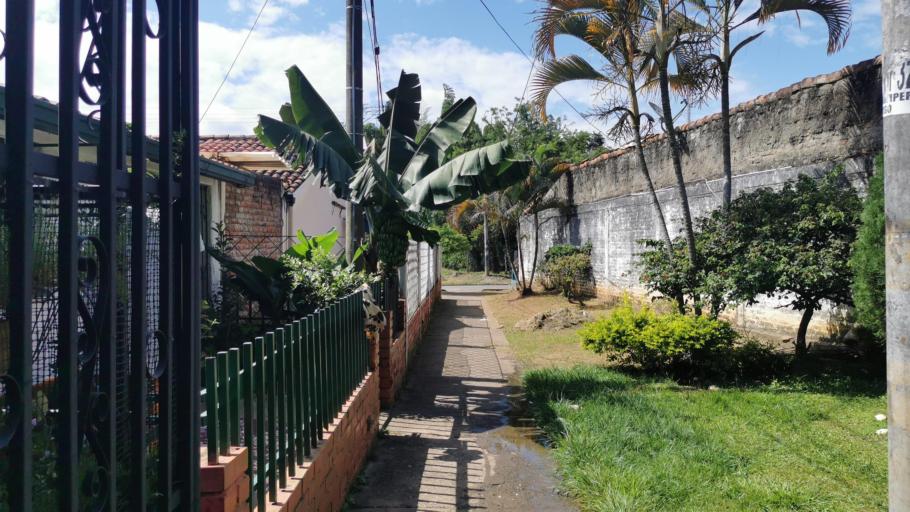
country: CO
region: Valle del Cauca
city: Jamundi
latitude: 3.2635
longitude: -76.5365
